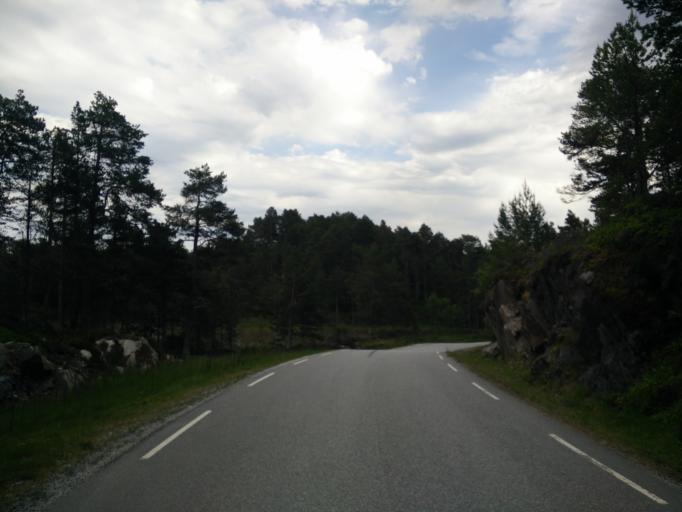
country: NO
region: More og Romsdal
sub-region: Kristiansund
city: Rensvik
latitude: 63.0327
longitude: 7.9543
